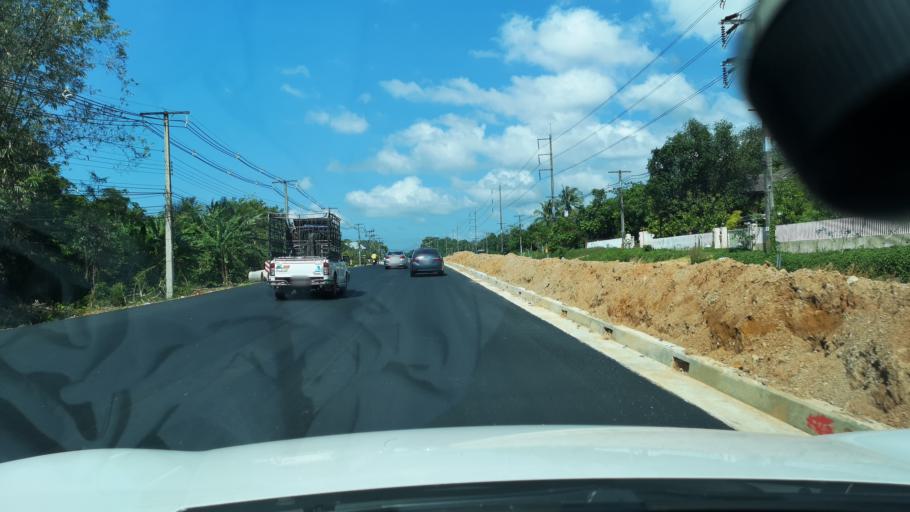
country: TH
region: Phangnga
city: Thai Mueang
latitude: 8.4223
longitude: 98.2588
